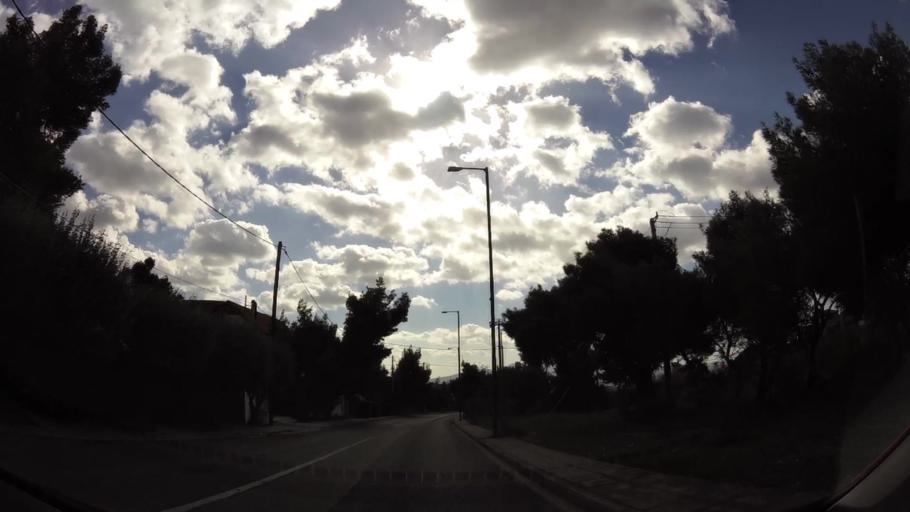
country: GR
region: Attica
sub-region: Nomarchia Anatolikis Attikis
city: Thrakomakedones
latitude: 38.1224
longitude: 23.7525
